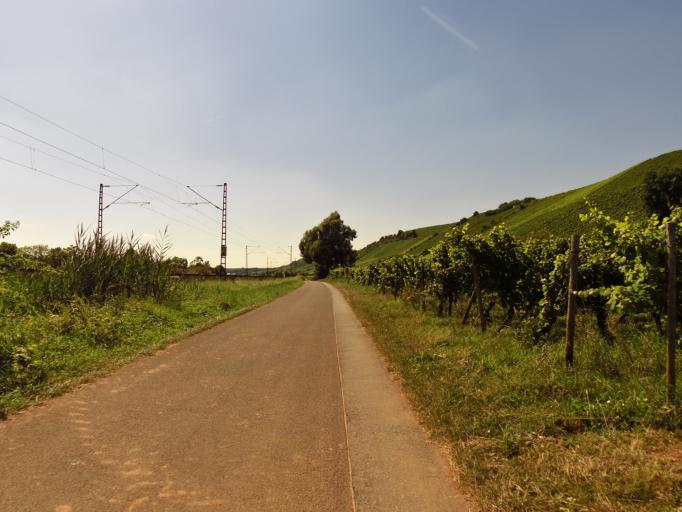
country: DE
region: Rheinland-Pfalz
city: Nackenheim
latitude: 49.8993
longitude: 8.3417
